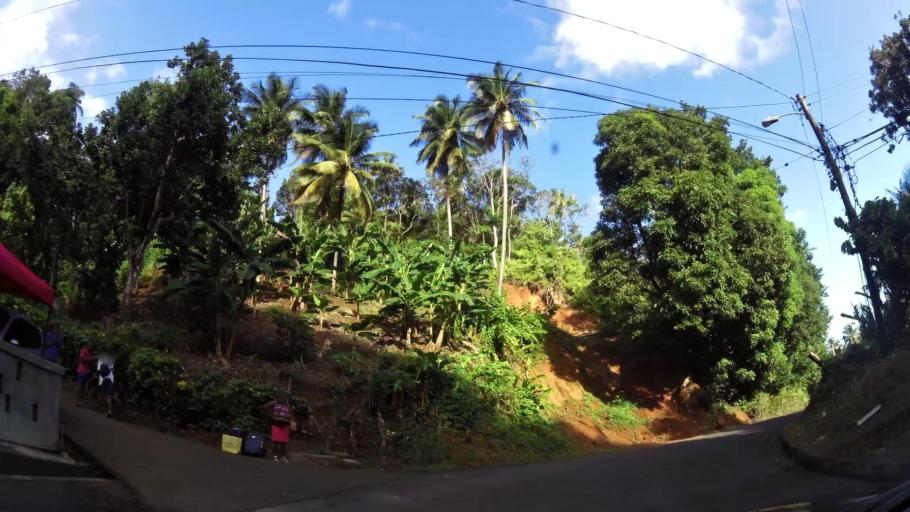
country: DM
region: Saint Andrew
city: Calibishie
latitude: 15.5912
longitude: -61.3821
